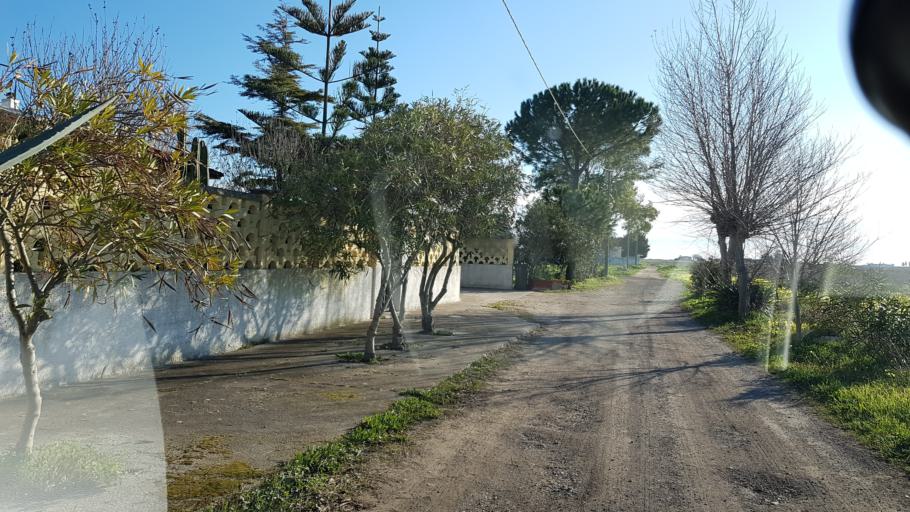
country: IT
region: Apulia
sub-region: Provincia di Brindisi
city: Tuturano
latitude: 40.5420
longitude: 17.9587
